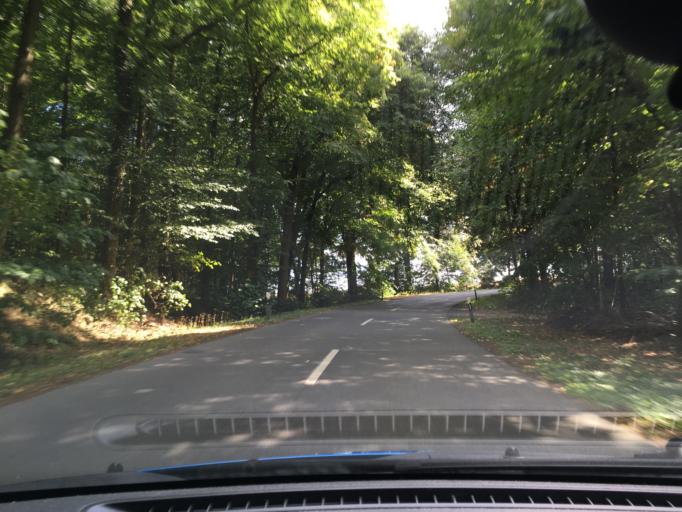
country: DE
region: Lower Saxony
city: Rehlingen
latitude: 53.0753
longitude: 10.2321
